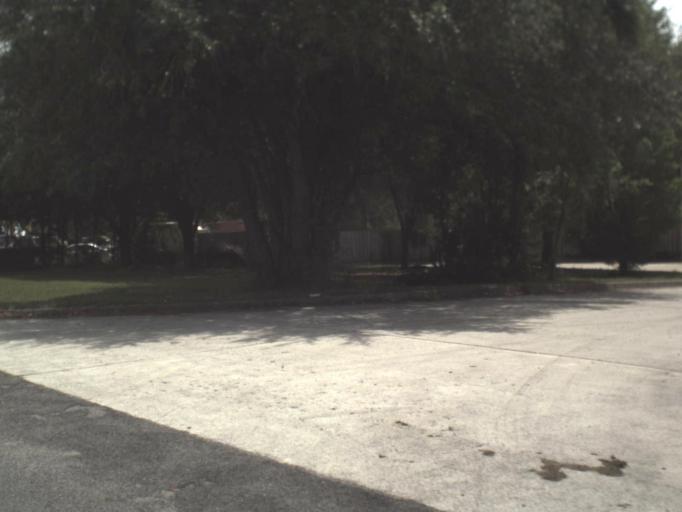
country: US
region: Florida
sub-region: Nassau County
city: Yulee
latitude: 30.6213
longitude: -81.5988
